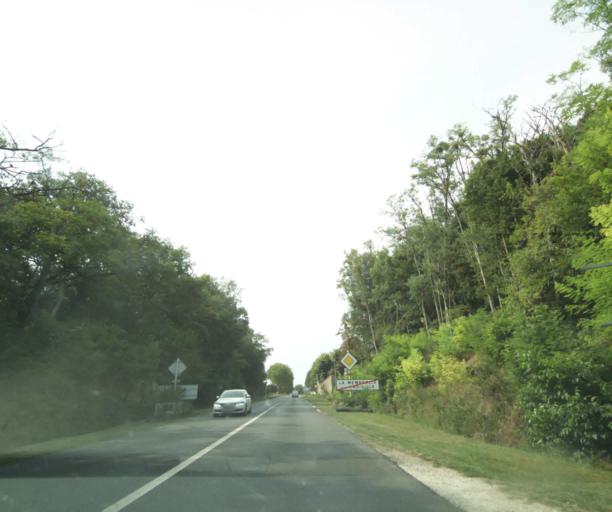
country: FR
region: Centre
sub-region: Departement d'Indre-et-Loire
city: La Membrolle-sur-Choisille
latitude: 47.4436
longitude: 0.6358
